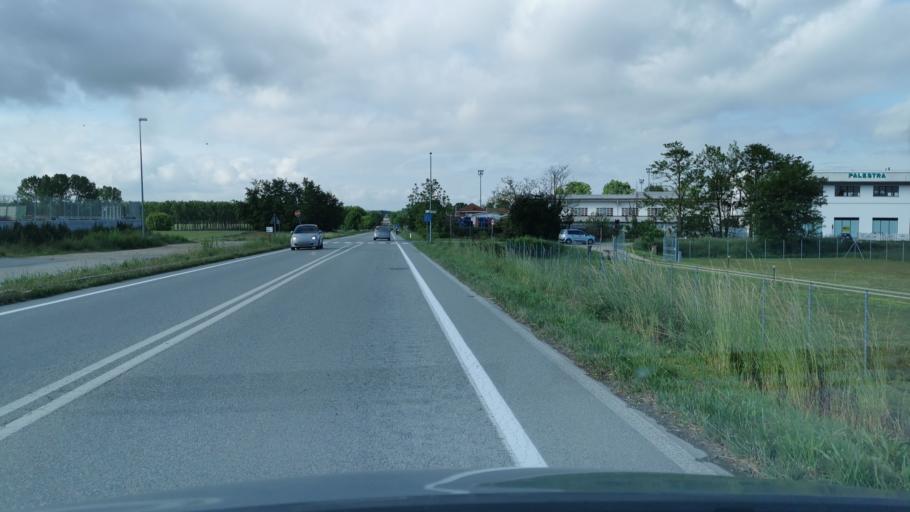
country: IT
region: Piedmont
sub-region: Provincia di Torino
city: Santena
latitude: 44.9528
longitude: 7.7857
